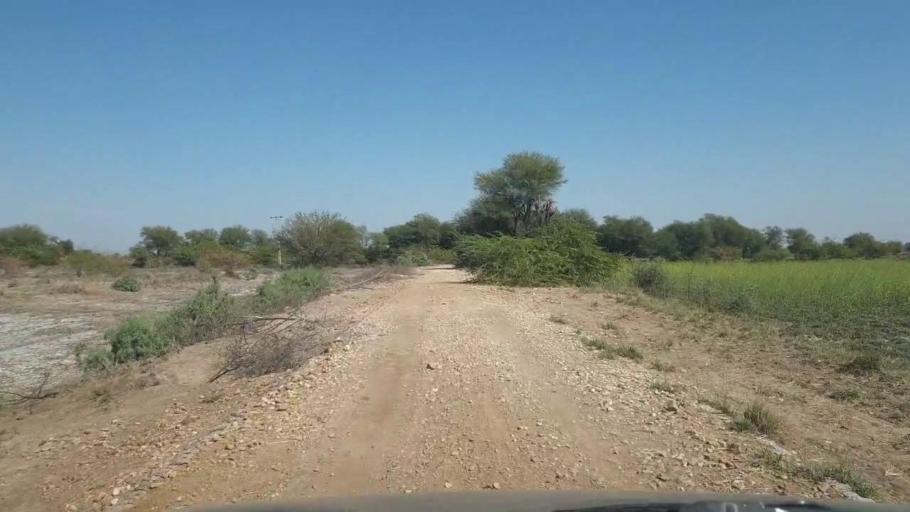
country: PK
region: Sindh
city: Dhoro Naro
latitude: 25.4351
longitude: 69.6191
